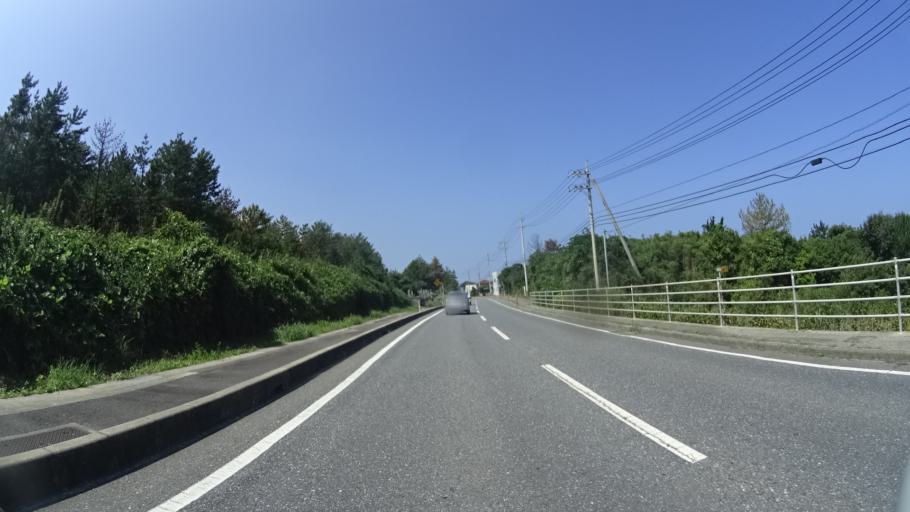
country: JP
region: Shimane
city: Masuda
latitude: 34.6876
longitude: 131.8001
